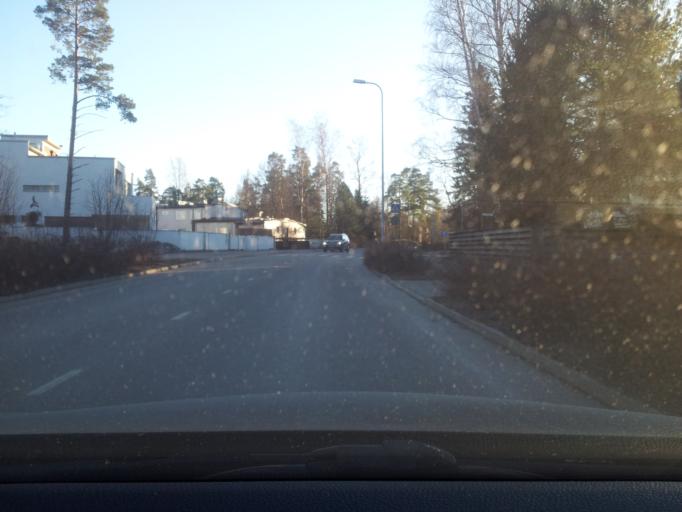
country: FI
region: Uusimaa
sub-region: Helsinki
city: Otaniemi
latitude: 60.1654
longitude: 24.8055
